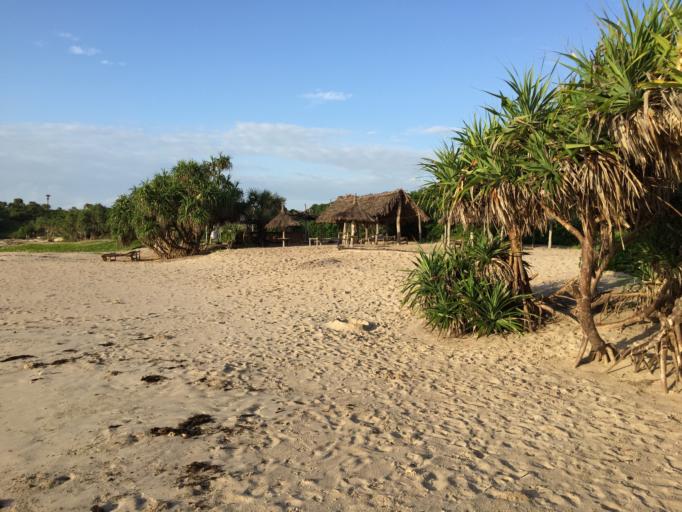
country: TZ
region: Pwani
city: Vikindu
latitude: -7.0154
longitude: 39.5492
